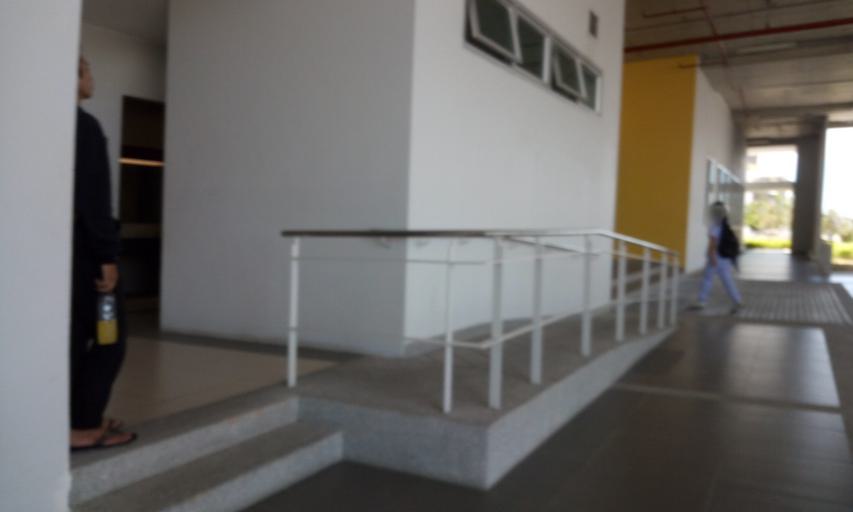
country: TH
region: Samut Prakan
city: Bang Bo District
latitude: 13.5261
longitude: 100.7600
